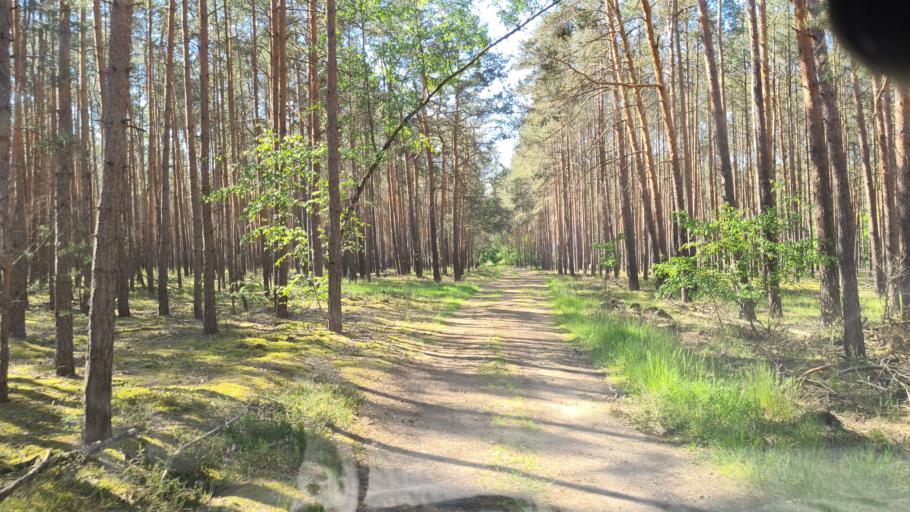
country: DE
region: Brandenburg
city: Ruckersdorf
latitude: 51.6074
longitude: 13.6190
